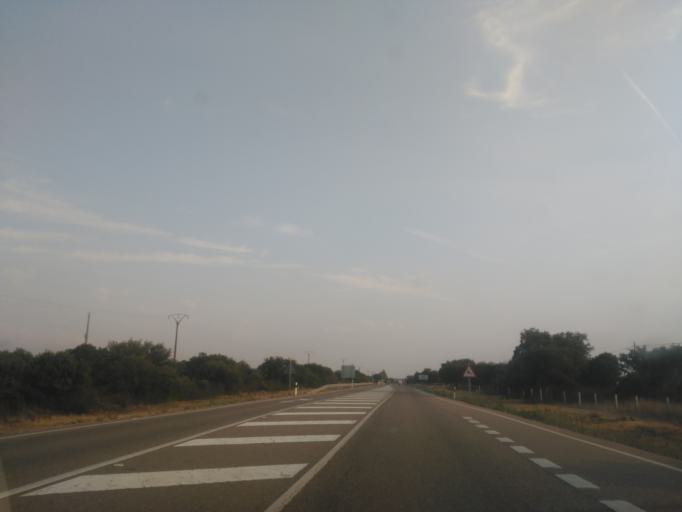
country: ES
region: Castille and Leon
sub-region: Provincia de Zamora
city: San Cebrian de Castro
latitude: 41.7145
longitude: -5.8092
